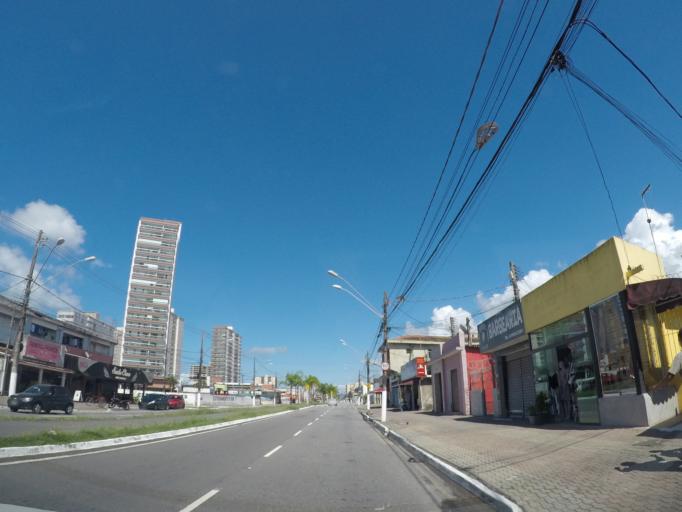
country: BR
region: Sao Paulo
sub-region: Mongagua
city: Mongagua
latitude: -24.0454
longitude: -46.5266
